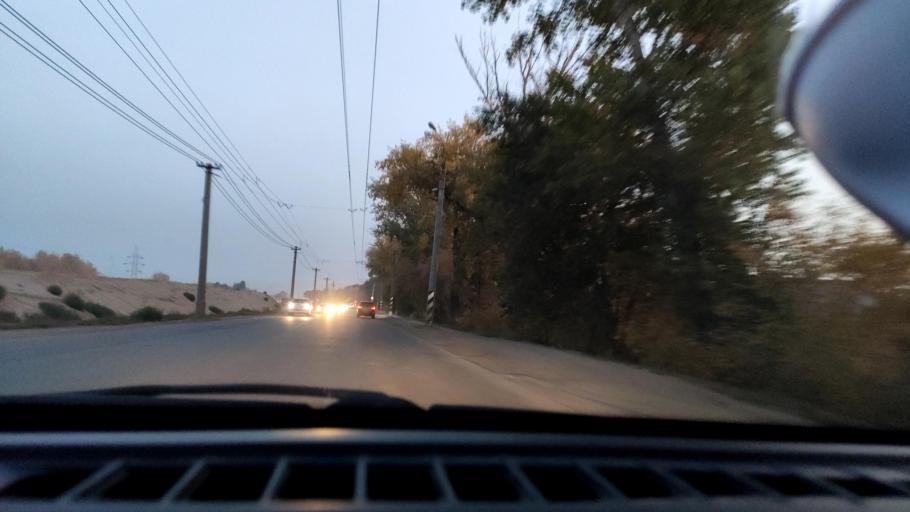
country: RU
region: Samara
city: Samara
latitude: 53.1454
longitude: 50.0965
